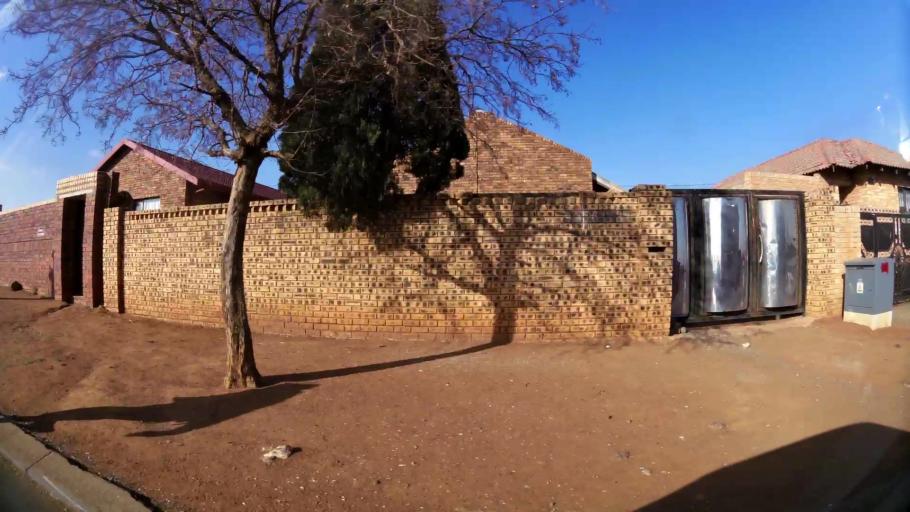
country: ZA
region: Gauteng
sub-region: City of Johannesburg Metropolitan Municipality
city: Soweto
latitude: -26.2655
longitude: 27.9169
